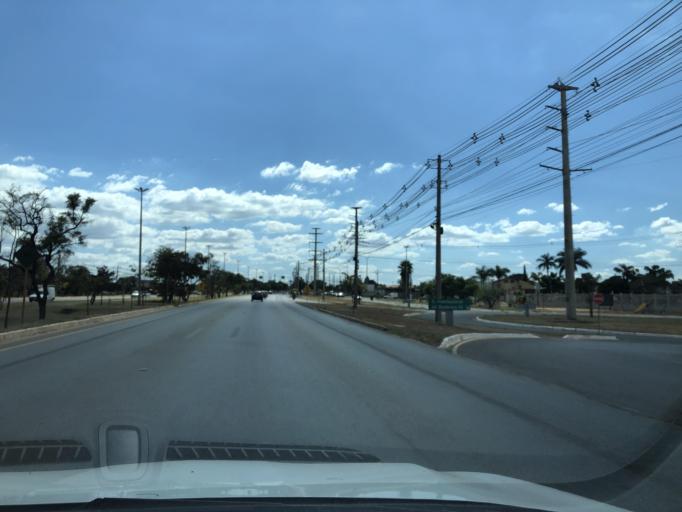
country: BR
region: Federal District
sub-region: Brasilia
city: Brasilia
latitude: -15.8833
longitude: -47.8222
